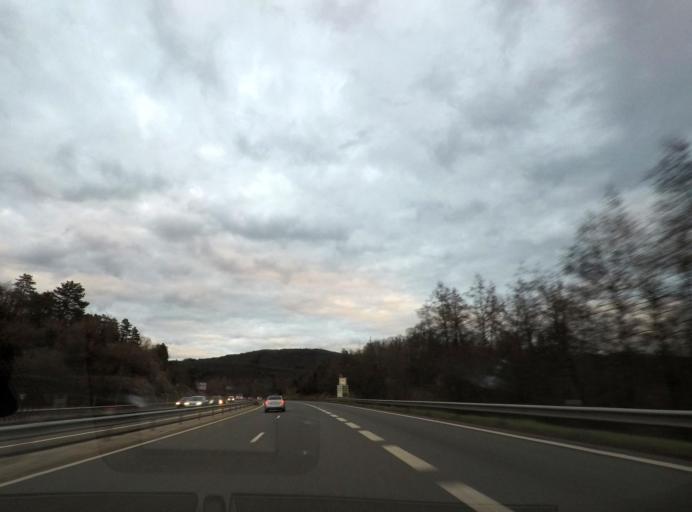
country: FR
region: Rhone-Alpes
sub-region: Departement de l'Ain
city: Poncin
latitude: 46.1124
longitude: 5.4803
